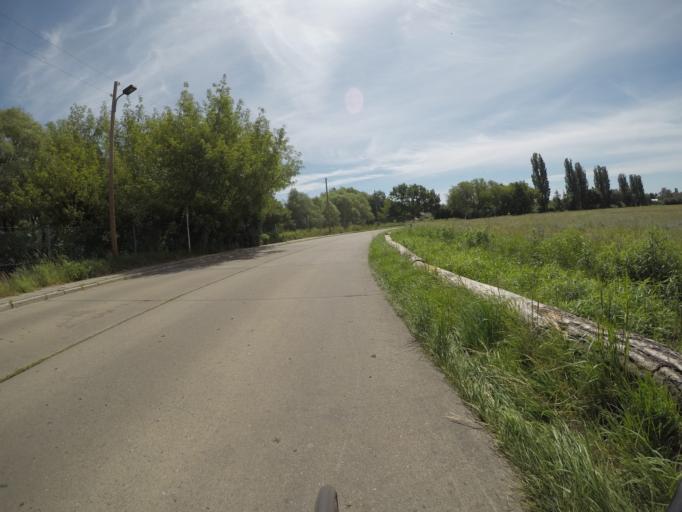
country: DE
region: Berlin
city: Mahlsdorf
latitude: 52.4971
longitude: 13.5989
